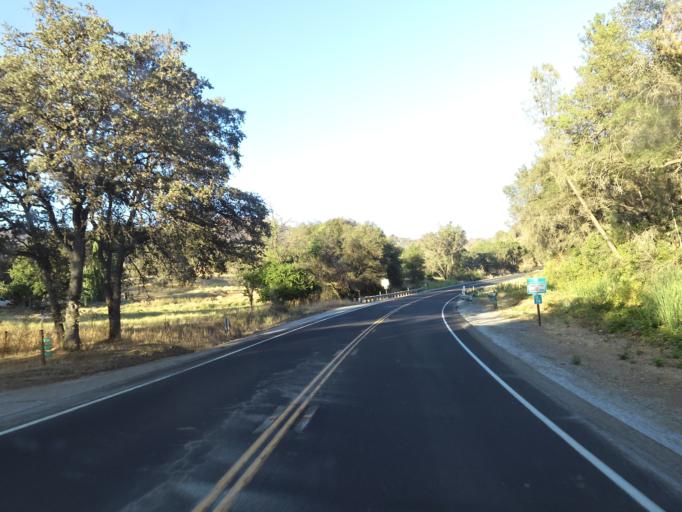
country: US
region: California
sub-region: Mariposa County
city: Mariposa
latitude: 37.4862
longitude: -119.9990
